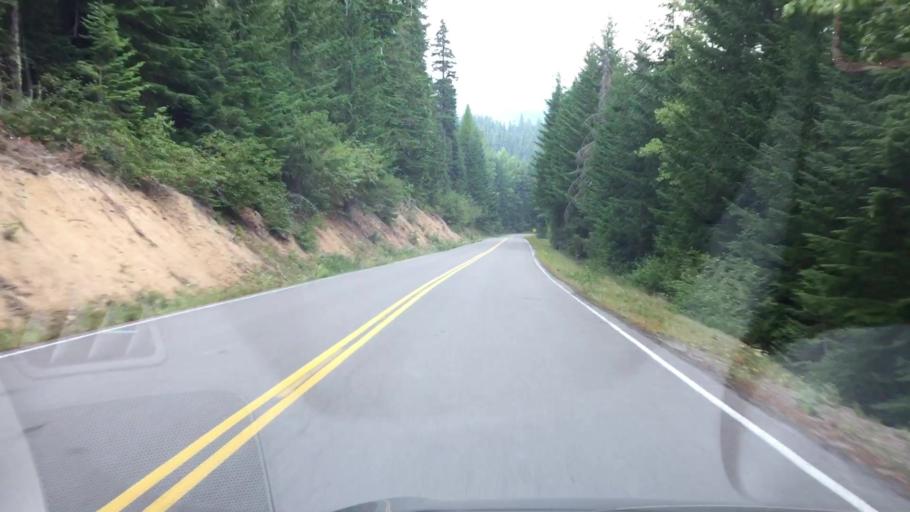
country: US
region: Washington
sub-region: Klickitat County
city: White Salmon
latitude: 46.1220
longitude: -121.6240
